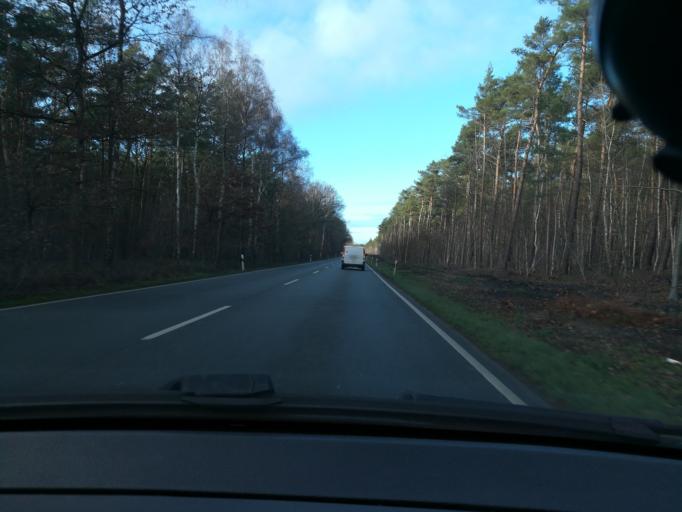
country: DE
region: Lower Saxony
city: Uchte
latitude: 52.5359
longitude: 8.8747
